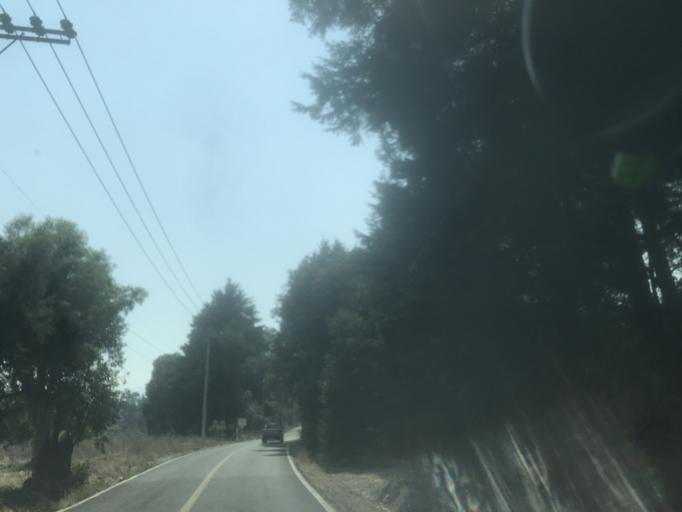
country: MX
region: Mexico
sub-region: Atlautla
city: San Juan Tepecoculco
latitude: 18.9977
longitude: -98.7776
